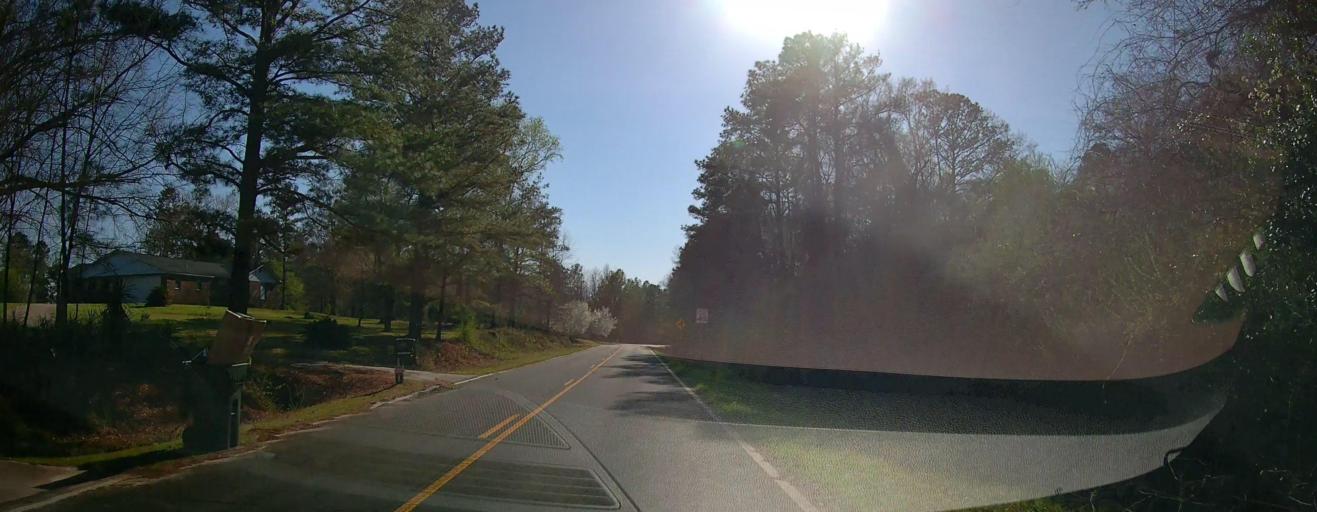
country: US
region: Georgia
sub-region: Peach County
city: Fort Valley
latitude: 32.5221
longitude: -83.9136
